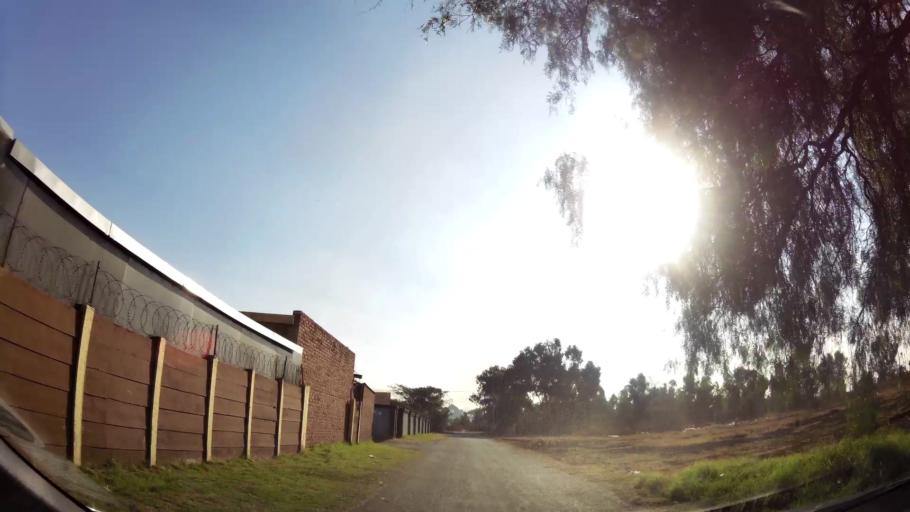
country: ZA
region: Gauteng
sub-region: Ekurhuleni Metropolitan Municipality
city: Brakpan
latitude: -26.2194
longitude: 28.3621
